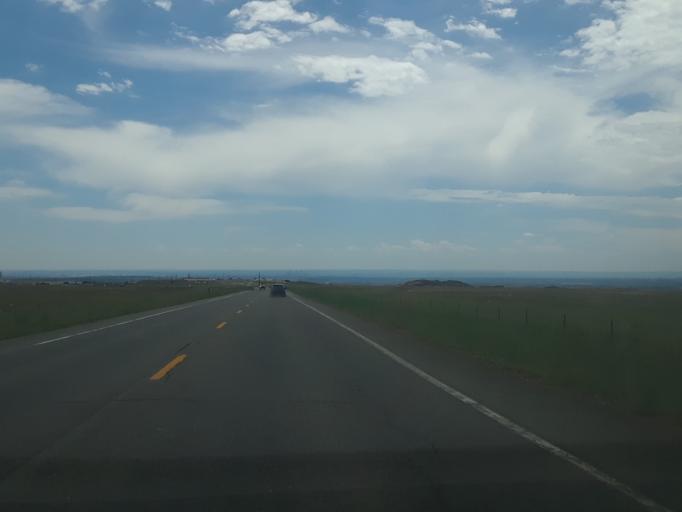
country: US
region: Colorado
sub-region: Jefferson County
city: Golden
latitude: 39.8687
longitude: -105.2547
